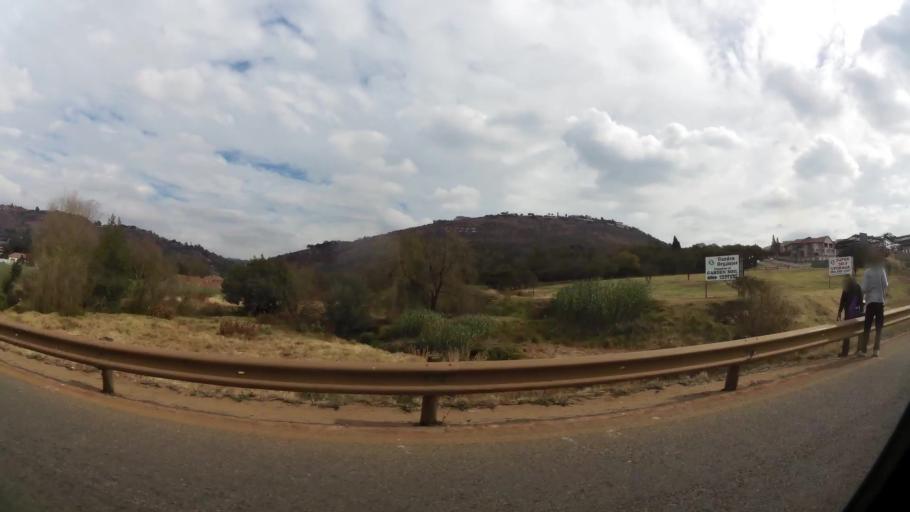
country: ZA
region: Gauteng
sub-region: City of Johannesburg Metropolitan Municipality
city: Roodepoort
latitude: -26.1072
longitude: 27.8821
